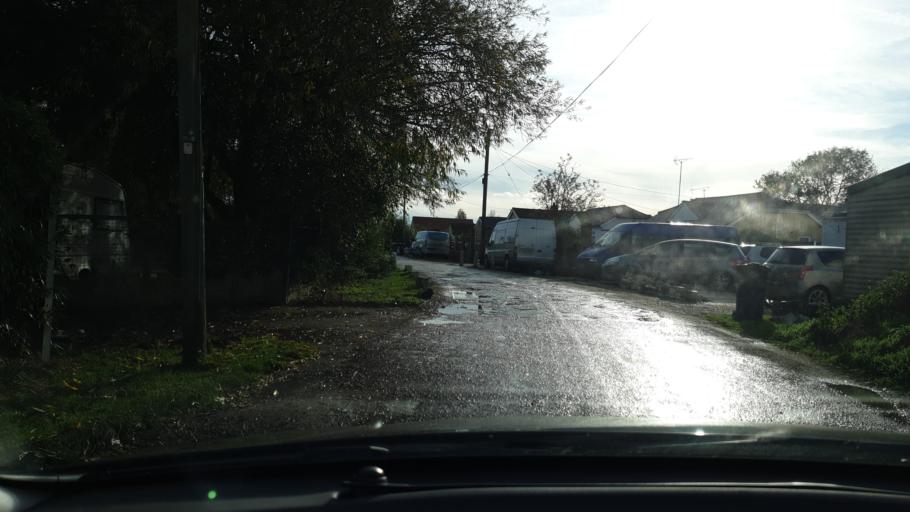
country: GB
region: England
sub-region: Essex
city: Saint Osyth
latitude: 51.7759
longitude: 1.0839
